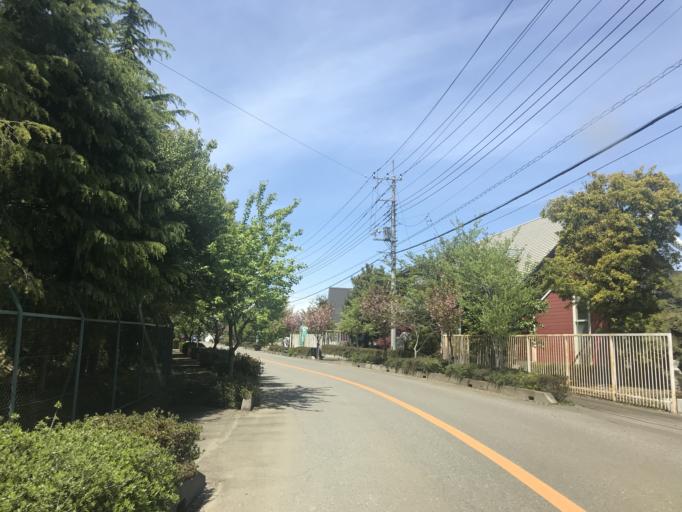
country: JP
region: Ibaraki
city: Shimodate
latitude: 36.2916
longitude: 140.0189
